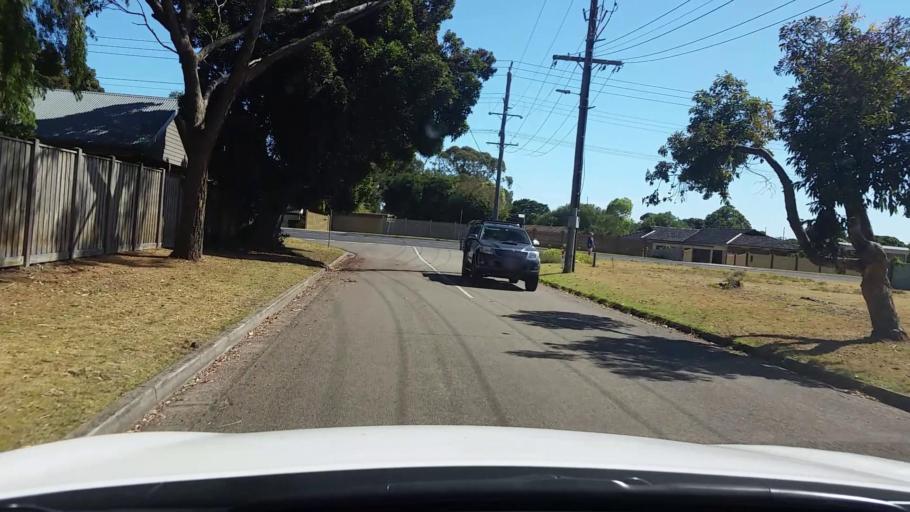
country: AU
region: Victoria
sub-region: Mornington Peninsula
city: Rosebud West
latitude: -38.3680
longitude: 144.8929
